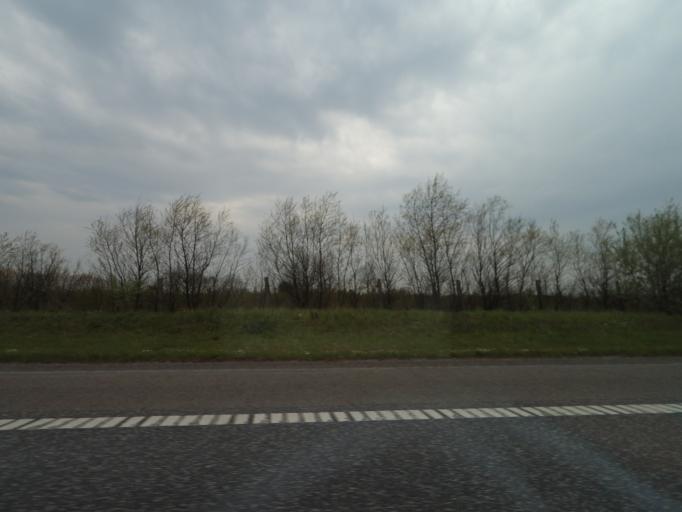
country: DK
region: South Denmark
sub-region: Faaborg-Midtfyn Kommune
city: Ringe
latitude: 55.2698
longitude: 10.4649
